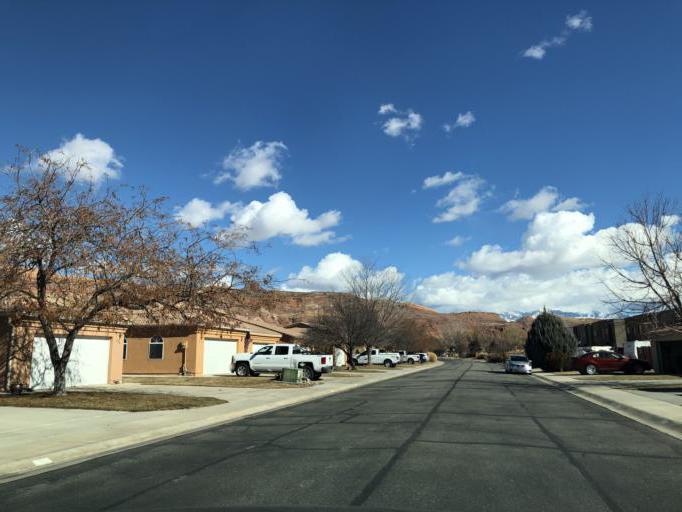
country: US
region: Utah
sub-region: Grand County
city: Moab
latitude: 38.5808
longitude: -109.5652
